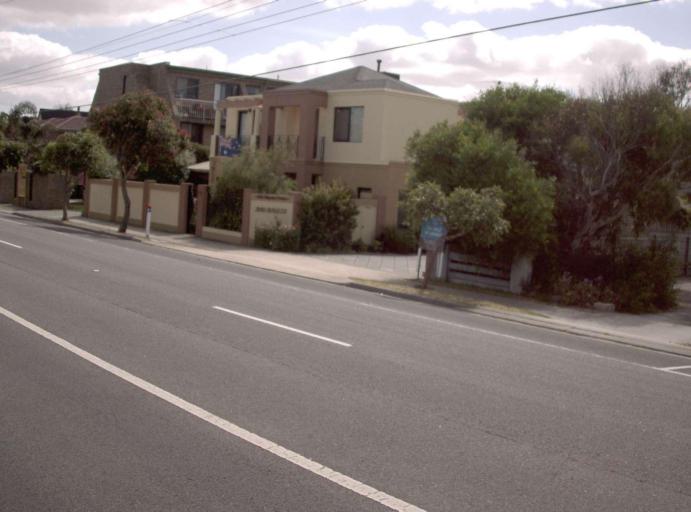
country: AU
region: Victoria
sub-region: Frankston
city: Frankston East
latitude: -38.1246
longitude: 145.1243
